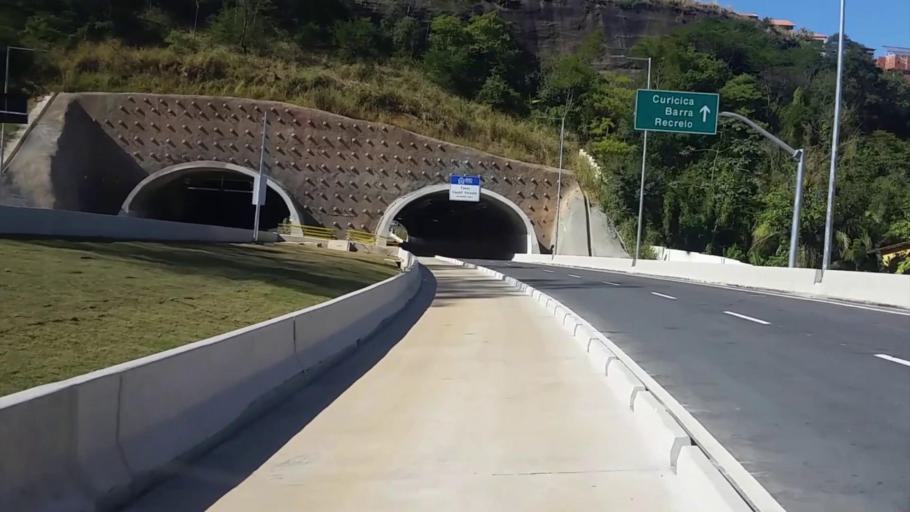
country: BR
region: Rio de Janeiro
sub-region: Nilopolis
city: Nilopolis
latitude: -22.9033
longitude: -43.3989
